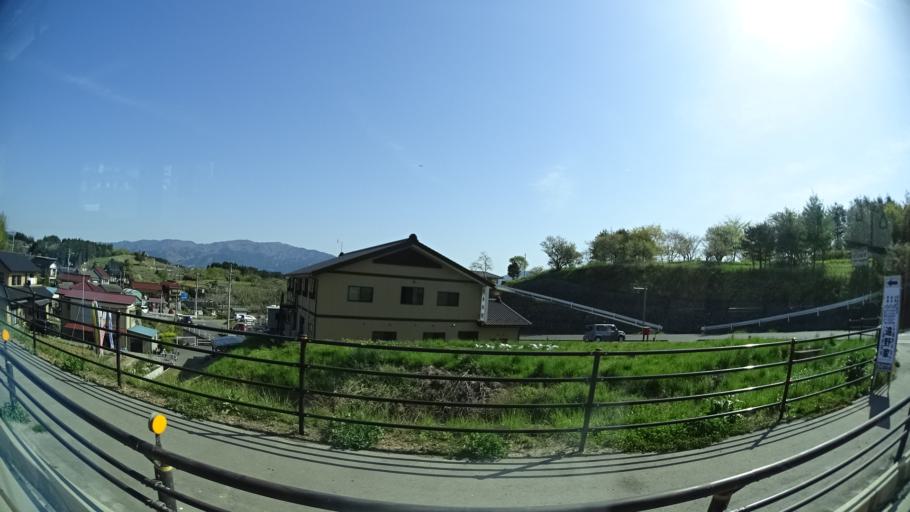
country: JP
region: Iwate
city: Ofunato
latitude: 38.9793
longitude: 141.6230
